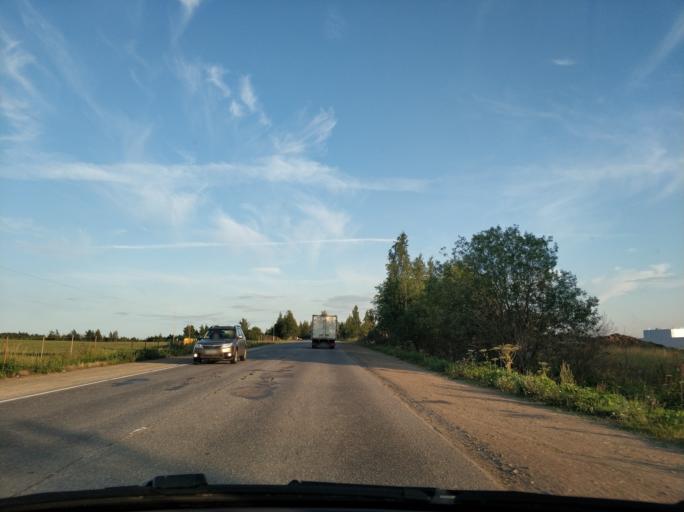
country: RU
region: Leningrad
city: Bugry
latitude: 60.0979
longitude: 30.3892
